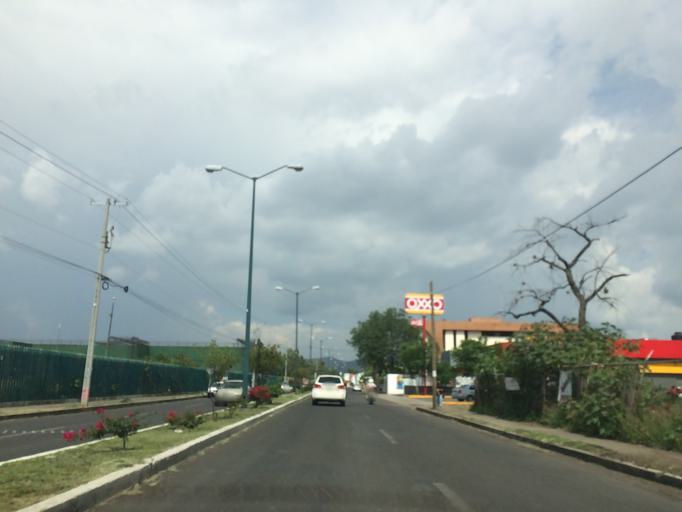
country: MX
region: Michoacan
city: Morelia
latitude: 19.6871
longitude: -101.2099
